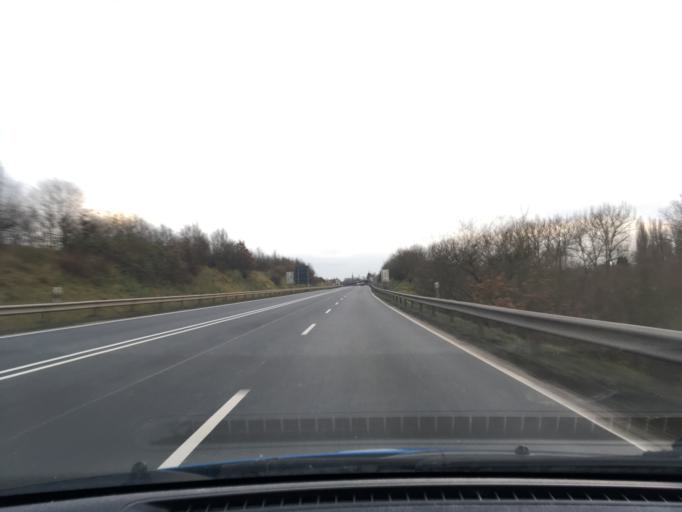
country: DE
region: Lower Saxony
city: Uelzen
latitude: 52.9812
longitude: 10.5683
